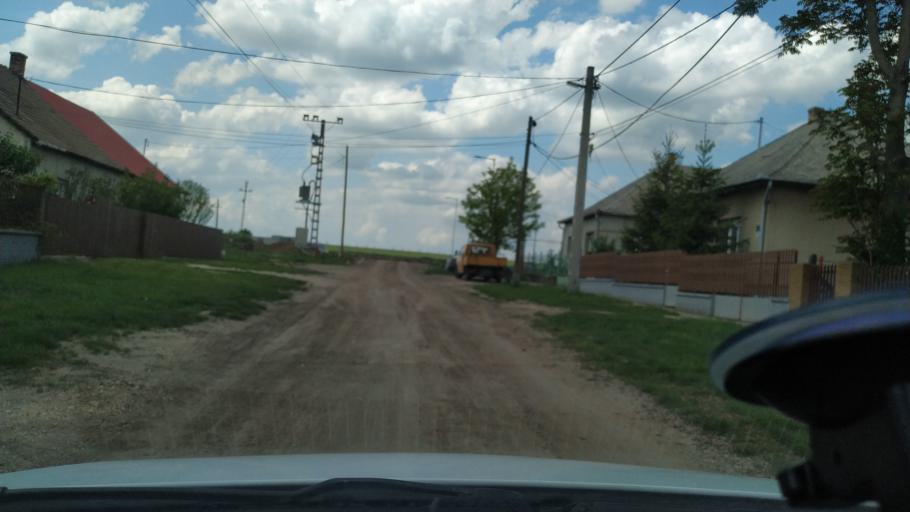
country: HU
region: Pest
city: Mende
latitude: 47.4330
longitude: 19.4522
